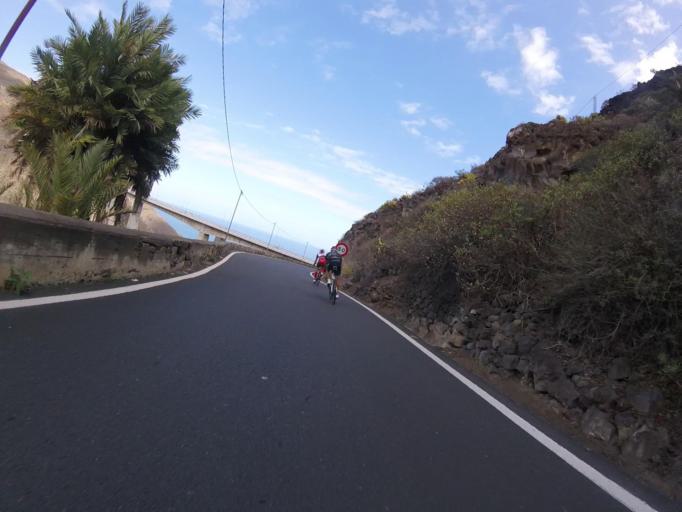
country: ES
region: Canary Islands
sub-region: Provincia de Las Palmas
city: Guia
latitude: 28.1380
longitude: -15.5967
